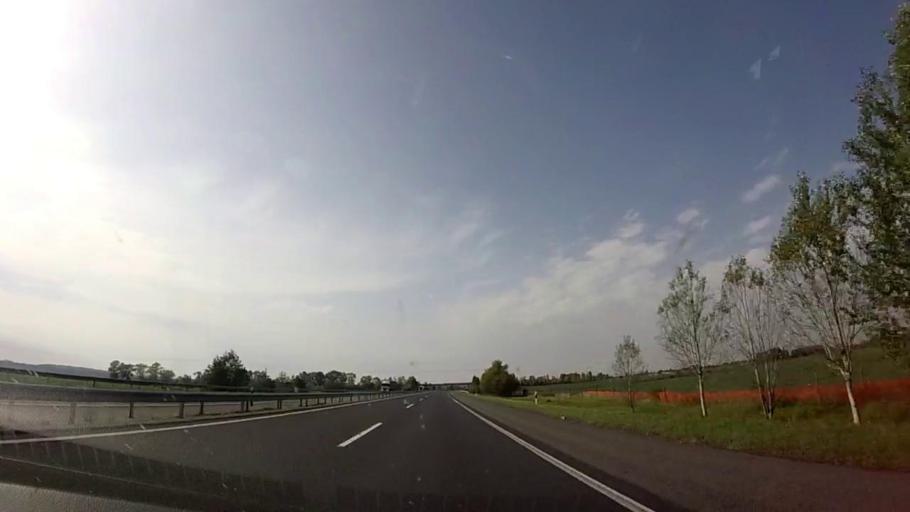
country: HU
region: Zala
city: Becsehely
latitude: 46.4204
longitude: 16.7695
